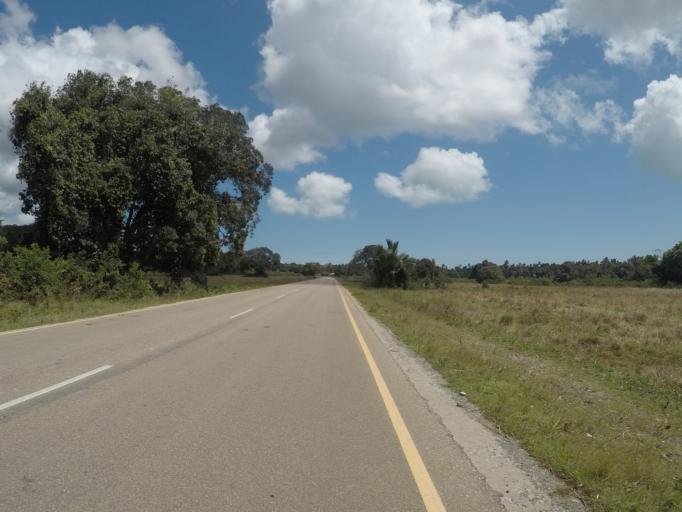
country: TZ
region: Zanzibar Central/South
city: Koani
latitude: -6.2278
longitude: 39.3604
